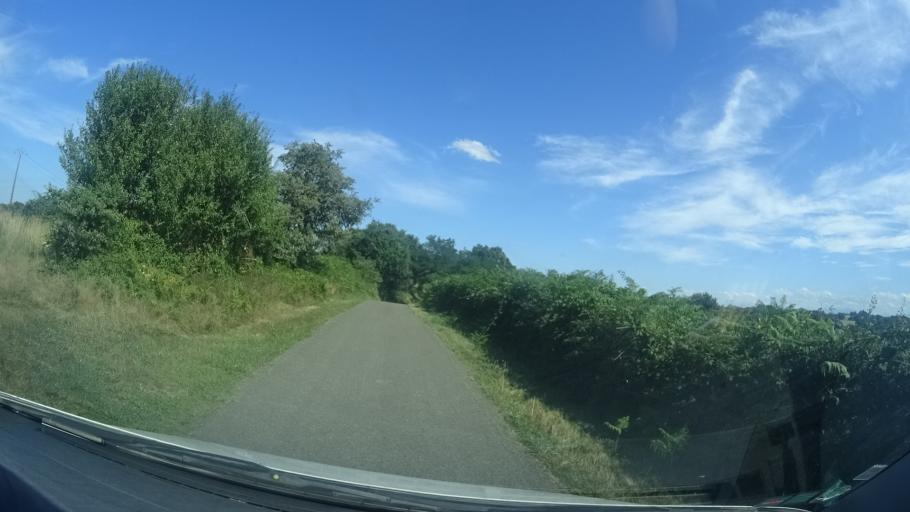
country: FR
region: Aquitaine
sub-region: Departement des Pyrenees-Atlantiques
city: Mont
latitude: 43.5048
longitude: -0.6826
